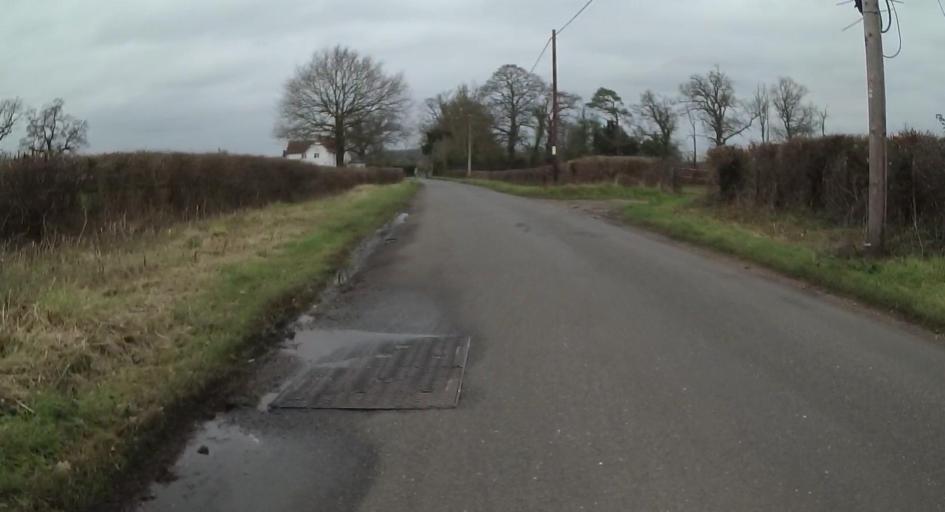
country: GB
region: England
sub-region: West Berkshire
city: Stratfield Mortimer
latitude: 51.3786
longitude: -1.0387
